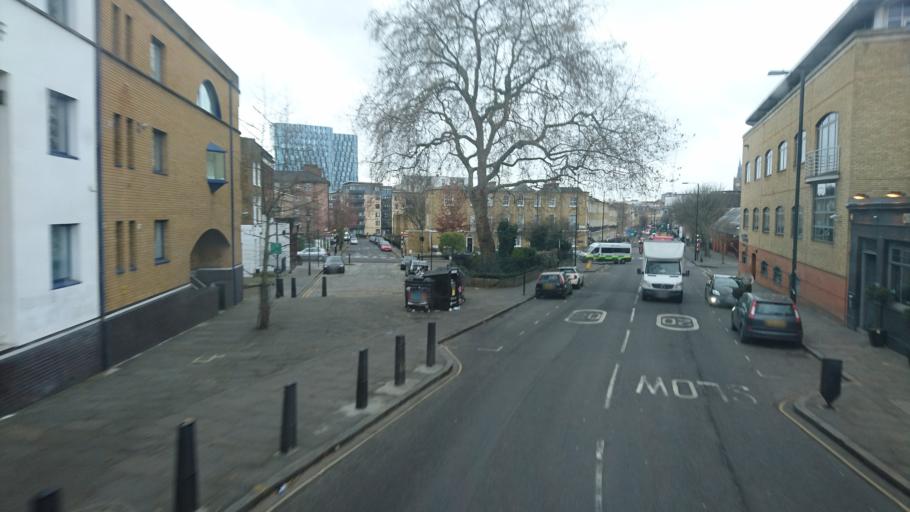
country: GB
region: England
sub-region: Greater London
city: Barnsbury
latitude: 51.5349
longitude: -0.1170
